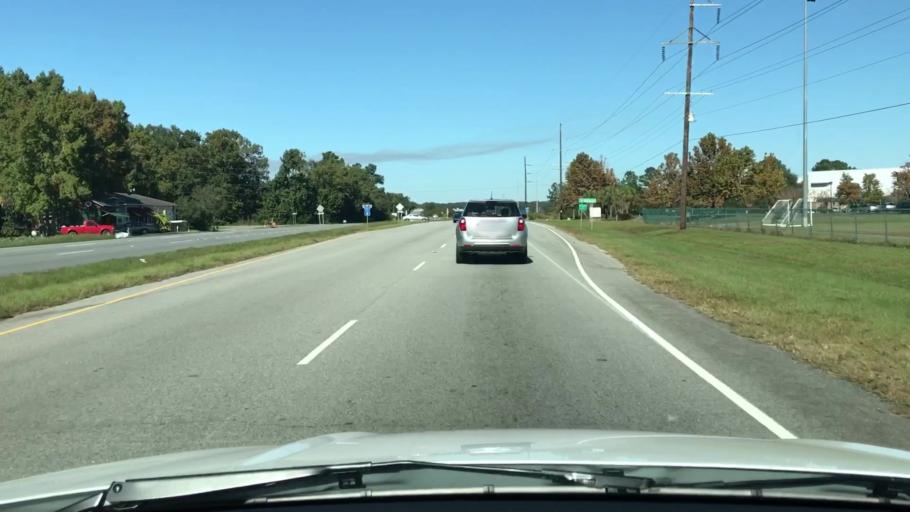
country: US
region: South Carolina
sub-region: Beaufort County
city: Laurel Bay
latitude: 32.5324
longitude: -80.7470
